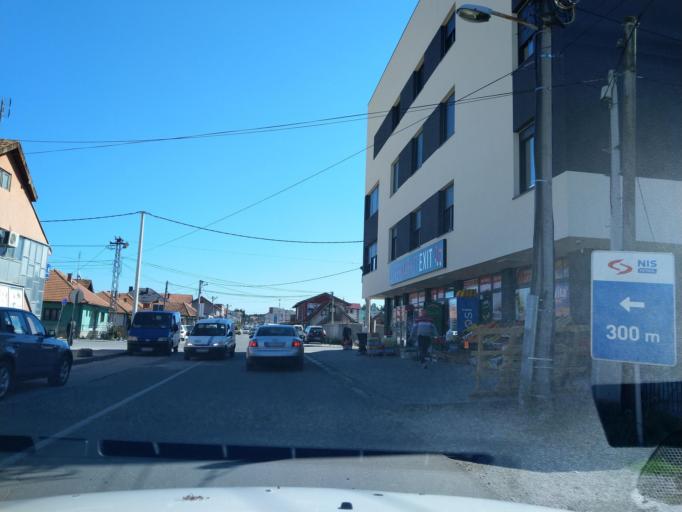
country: RS
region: Central Serbia
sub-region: Zlatiborski Okrug
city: Sjenica
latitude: 43.2744
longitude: 20.0045
